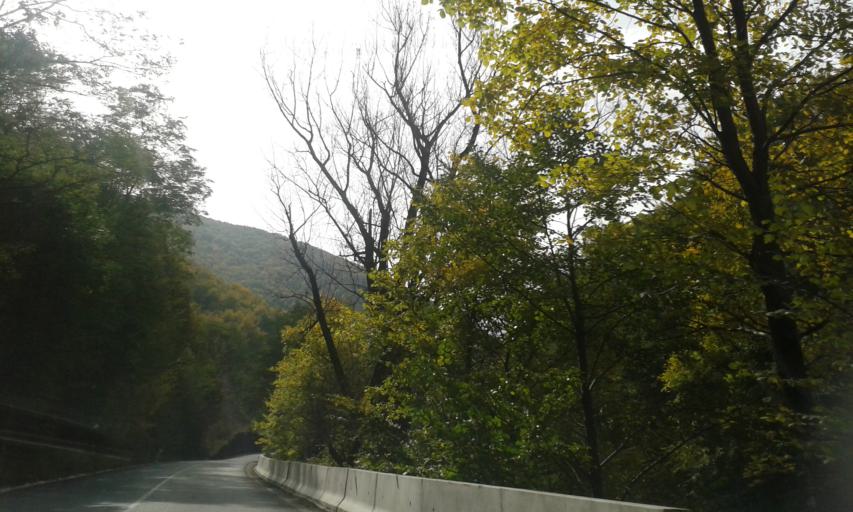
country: RO
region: Gorj
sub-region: Comuna Bumbesti-Jiu
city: Bumbesti-Jiu
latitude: 45.2324
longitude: 23.3908
